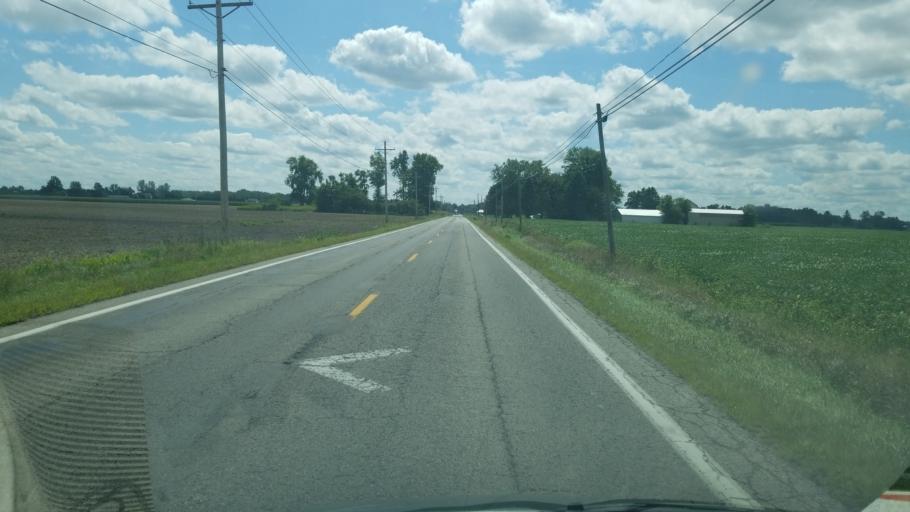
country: US
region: Ohio
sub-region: Henry County
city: Liberty Center
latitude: 41.4650
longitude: -84.0088
